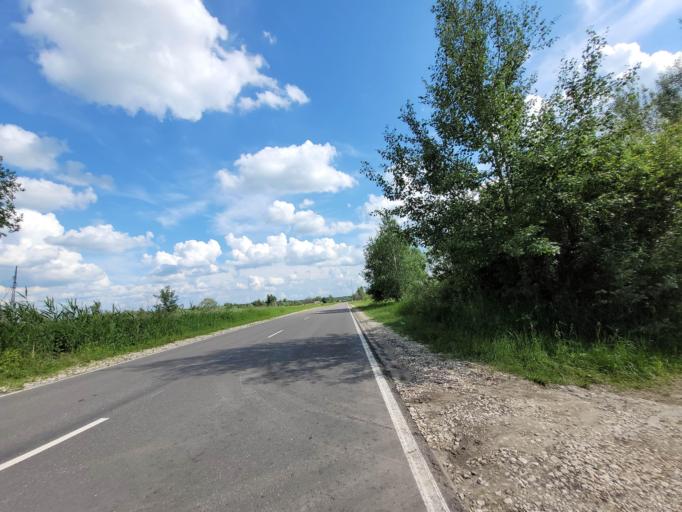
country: RU
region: Moskovskaya
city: Konobeyevo
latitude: 55.3962
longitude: 38.6832
